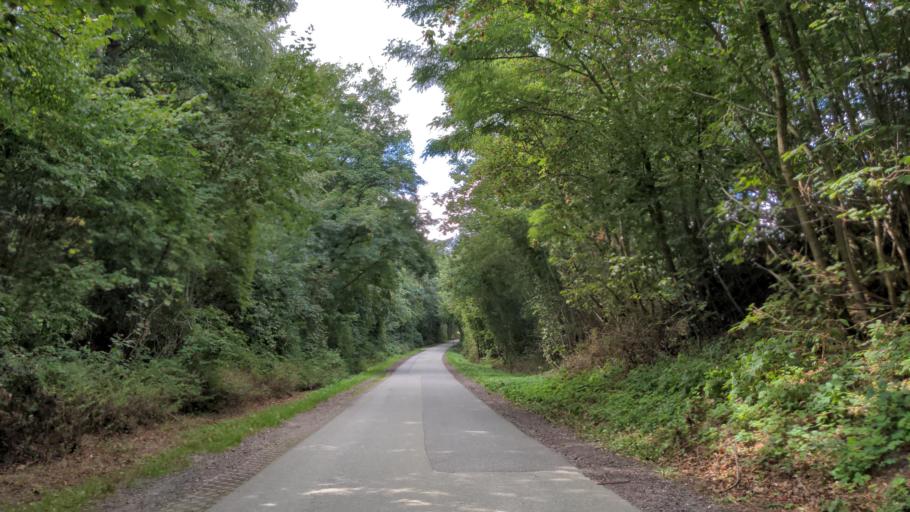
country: DE
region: Schleswig-Holstein
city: Kasseedorf
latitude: 54.1678
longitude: 10.6993
